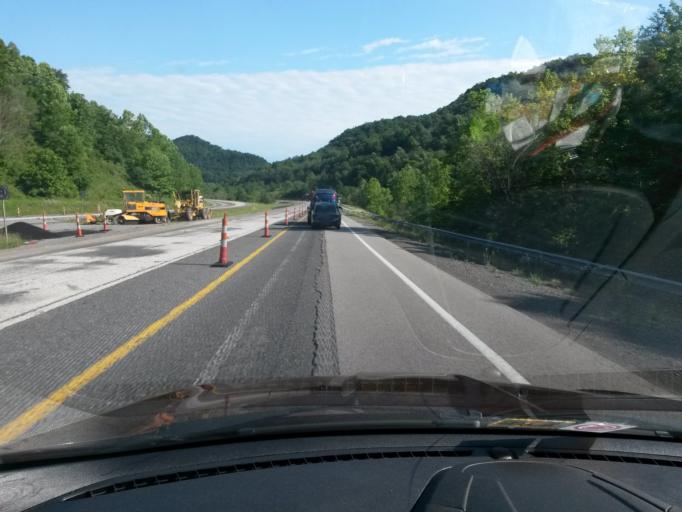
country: US
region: West Virginia
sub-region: Braxton County
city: Sutton
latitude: 38.7297
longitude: -80.6733
